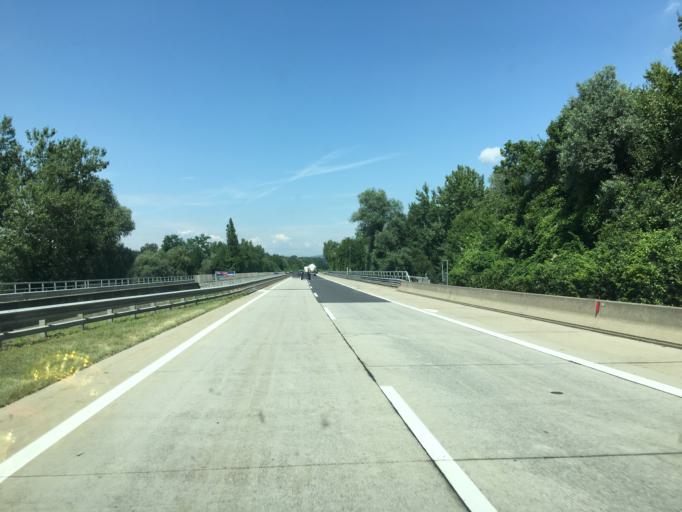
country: AT
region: Styria
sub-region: Politischer Bezirk Leibnitz
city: Gabersdorf
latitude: 46.7758
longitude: 15.5806
